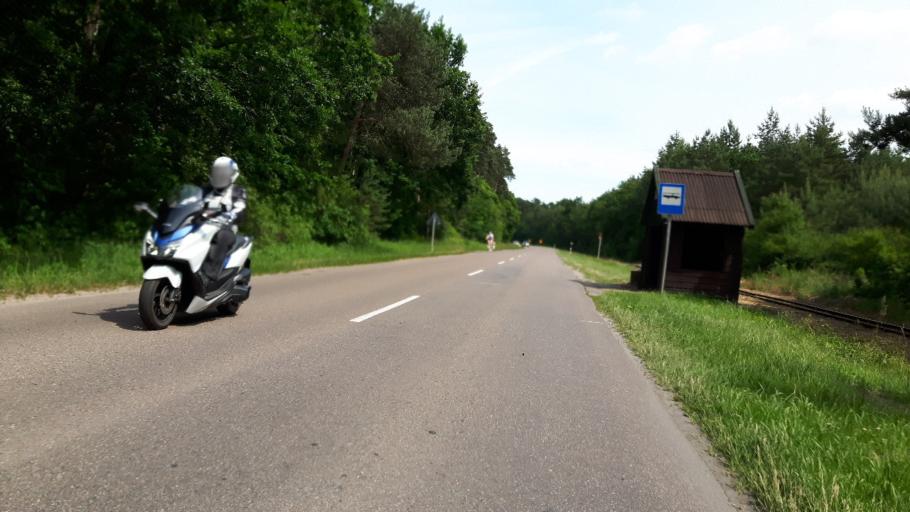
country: PL
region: Pomeranian Voivodeship
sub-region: Powiat nowodworski
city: Stegna
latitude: 54.3322
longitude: 19.0741
